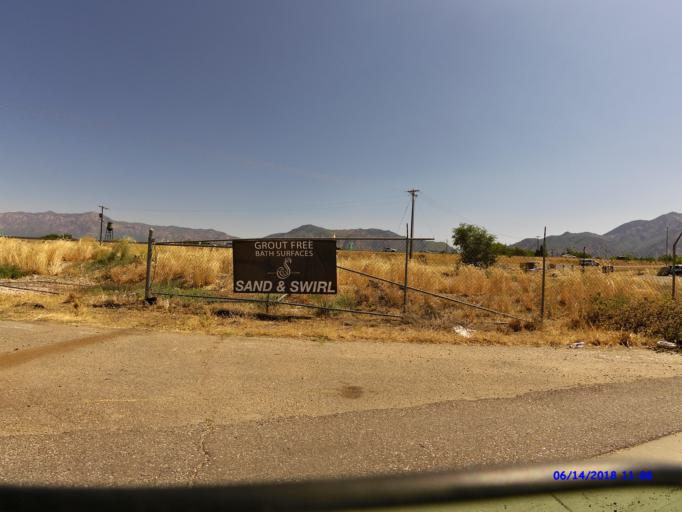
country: US
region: Utah
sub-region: Weber County
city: Ogden
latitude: 41.2170
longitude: -112.0046
